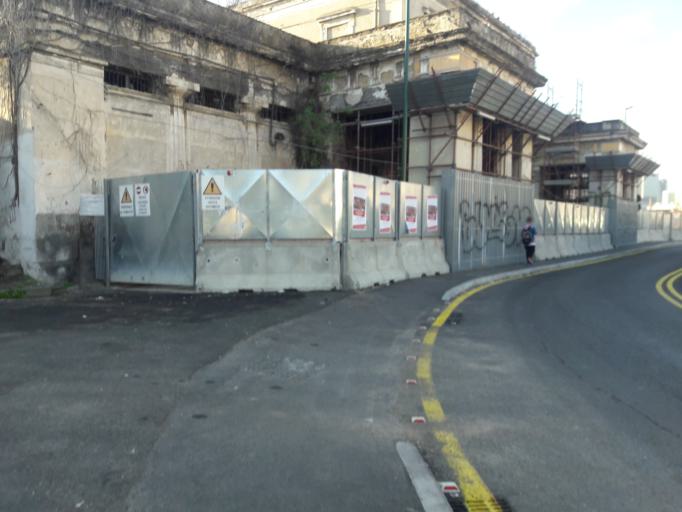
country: IT
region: Campania
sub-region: Provincia di Napoli
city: Arpino
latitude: 40.8667
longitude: 14.2922
